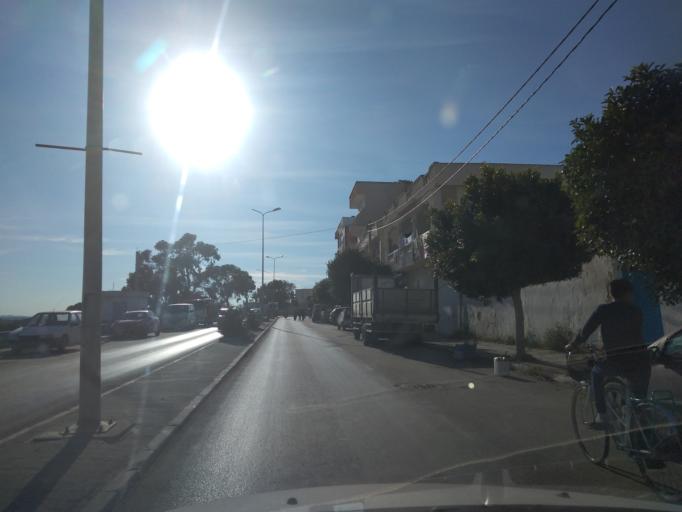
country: TN
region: Ariana
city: Qal'at al Andalus
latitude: 37.0576
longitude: 10.1087
